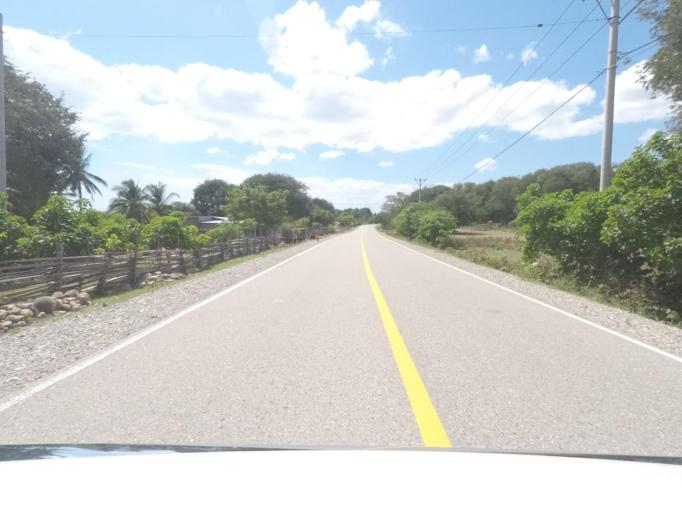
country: TL
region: Lautem
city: Lospalos
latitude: -8.4171
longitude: 126.7891
